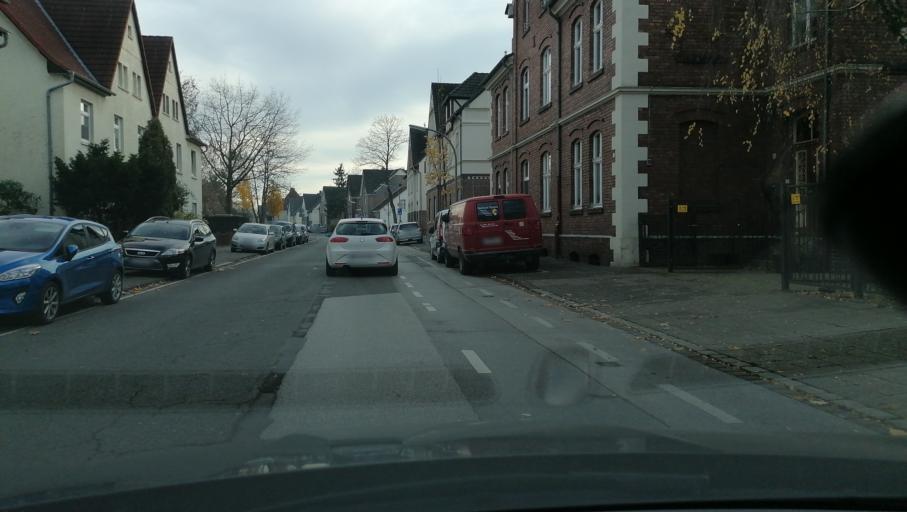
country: DE
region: North Rhine-Westphalia
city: Waltrop
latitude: 51.5669
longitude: 7.3747
